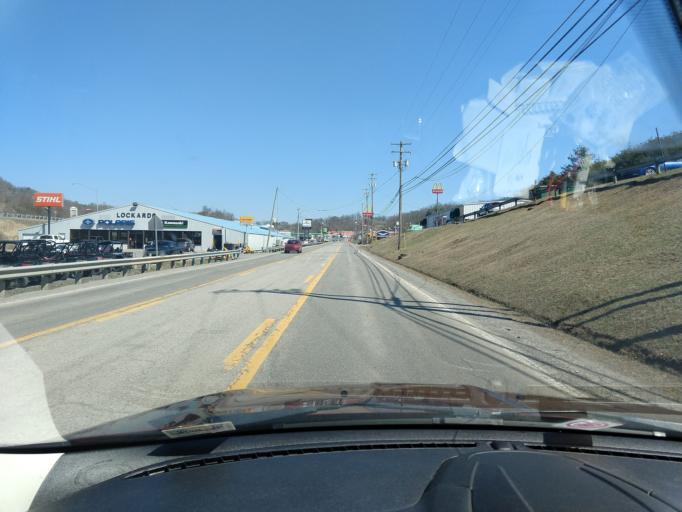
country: US
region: West Virginia
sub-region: Braxton County
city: Sutton
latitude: 38.6982
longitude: -80.6662
